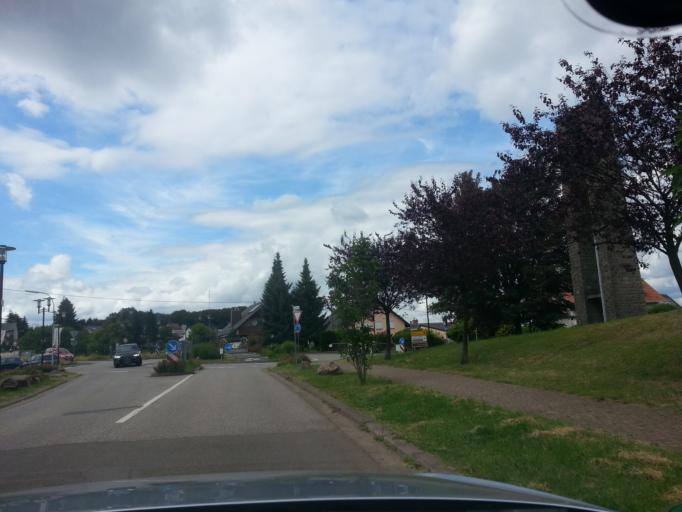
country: DE
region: Saarland
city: Orscholz
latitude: 49.5053
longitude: 6.5309
